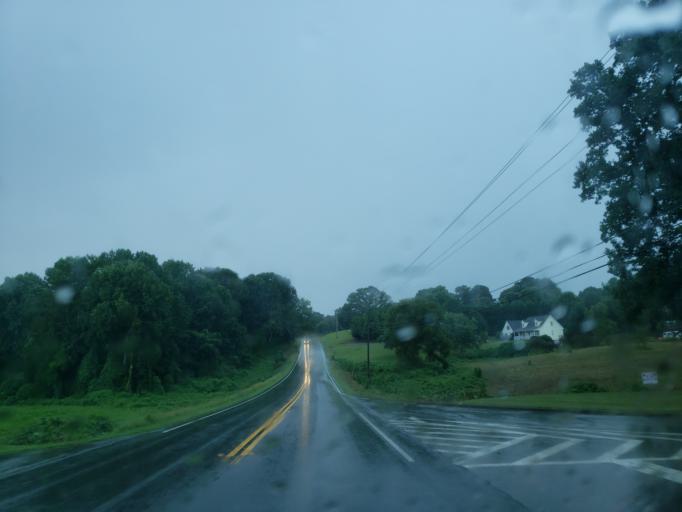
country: US
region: Georgia
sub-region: Cherokee County
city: Canton
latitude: 34.3087
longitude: -84.4610
